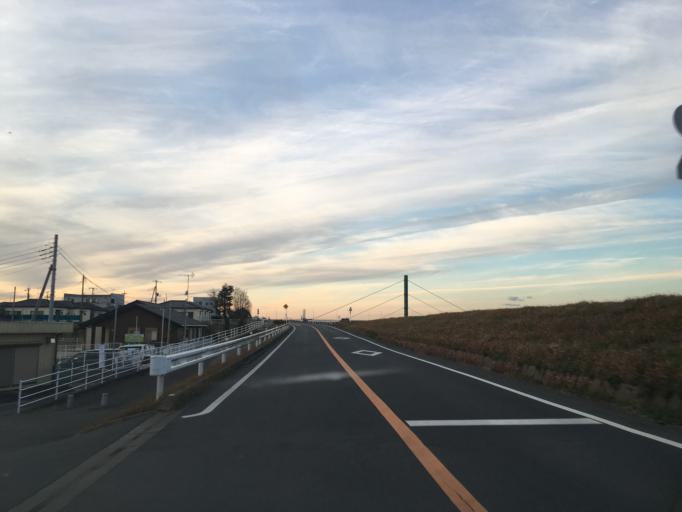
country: JP
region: Chiba
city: Katori-shi
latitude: 35.9047
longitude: 140.4959
